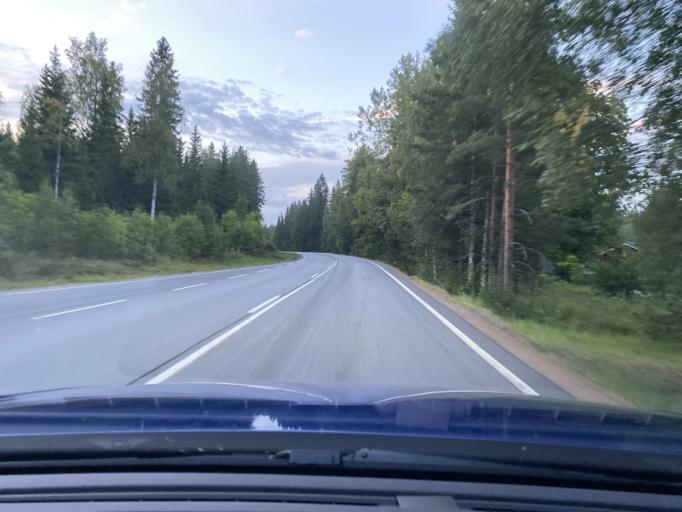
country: FI
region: Satakunta
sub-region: Pohjois-Satakunta
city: Honkajoki
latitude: 62.0518
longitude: 22.2493
